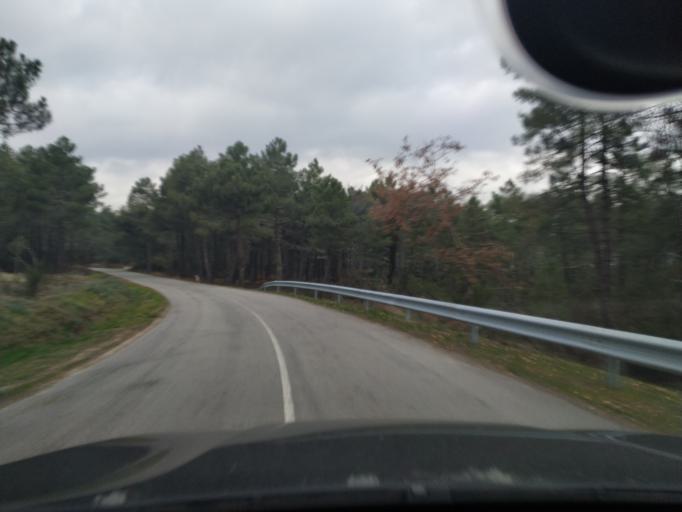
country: PT
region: Vila Real
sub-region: Sabrosa
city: Sabrosa
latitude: 41.3355
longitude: -7.6487
